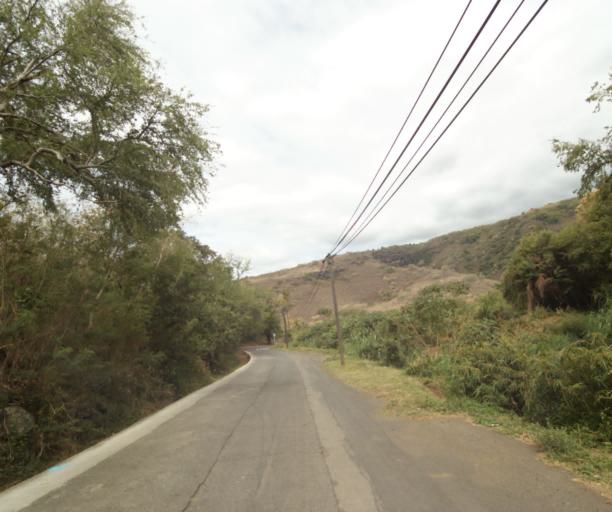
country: RE
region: Reunion
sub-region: Reunion
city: Saint-Paul
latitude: -20.9925
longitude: 55.3068
